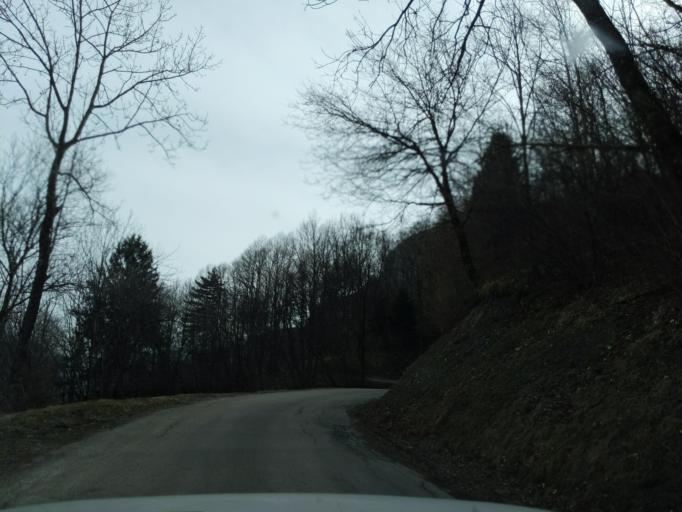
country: FR
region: Rhone-Alpes
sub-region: Departement de la Savoie
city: Villargondran
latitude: 45.2607
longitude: 6.3640
